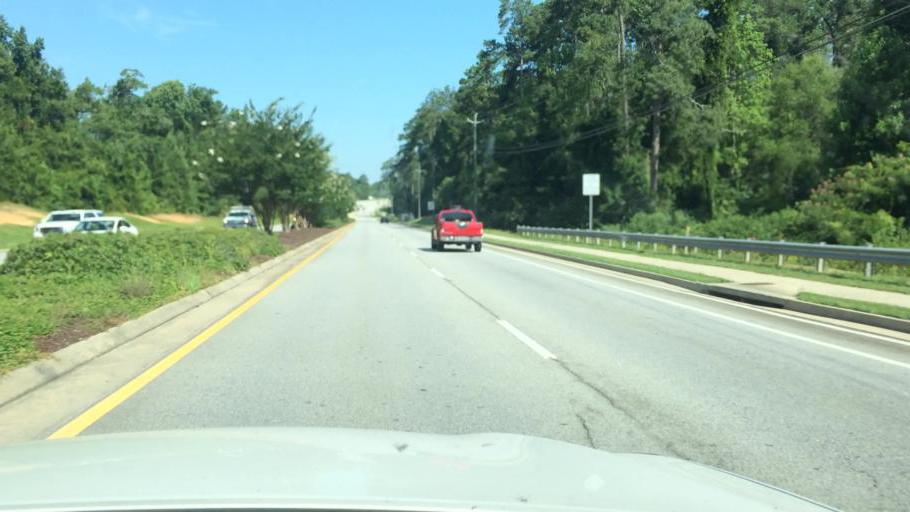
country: US
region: Georgia
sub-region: Columbia County
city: Martinez
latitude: 33.5206
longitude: -82.0639
